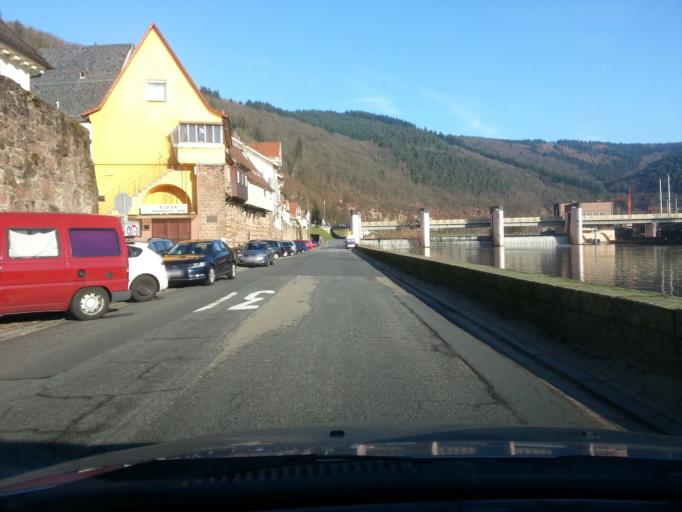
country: DE
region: Hesse
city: Hirschhorn
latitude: 49.4476
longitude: 8.8997
